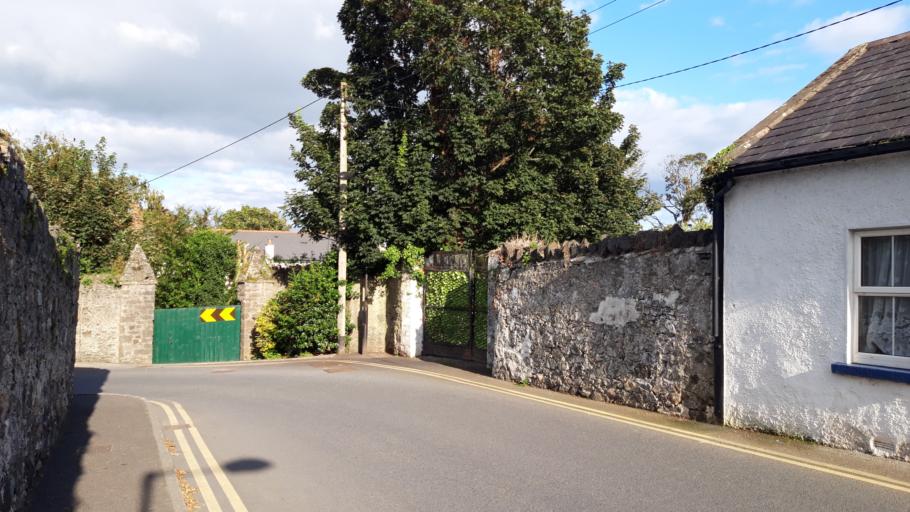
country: IE
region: Leinster
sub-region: Lu
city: Carlingford
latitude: 54.0391
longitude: -6.1848
